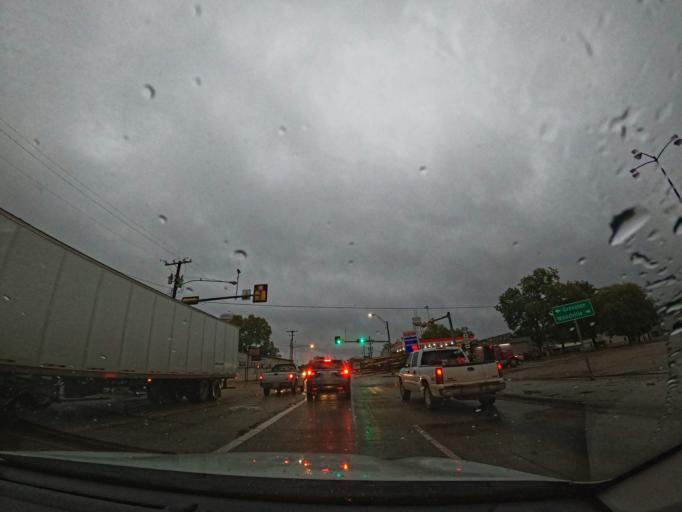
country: US
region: Texas
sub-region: Polk County
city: Corrigan
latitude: 30.9966
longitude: -94.8272
